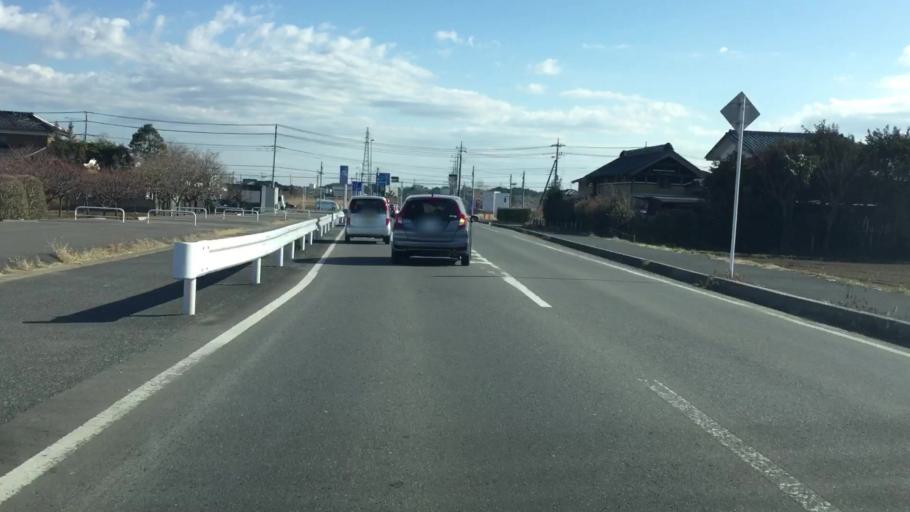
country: JP
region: Ibaraki
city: Fujishiro
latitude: 35.8456
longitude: 140.1324
